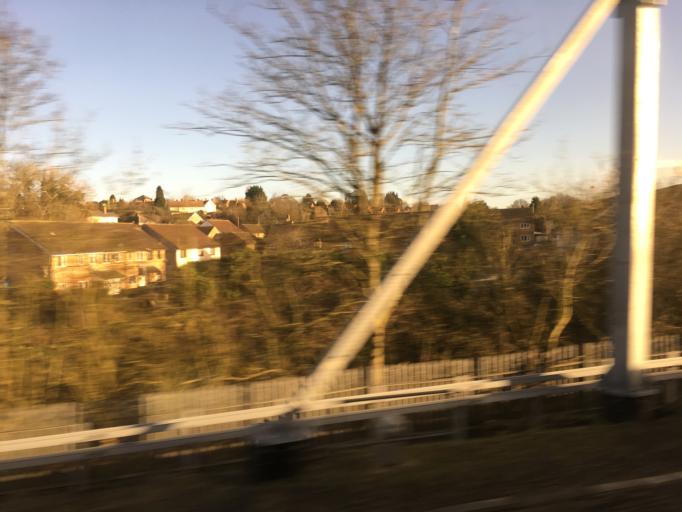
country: GB
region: England
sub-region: Wiltshire
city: Royal Wootton Bassett
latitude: 51.5358
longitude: -1.9085
